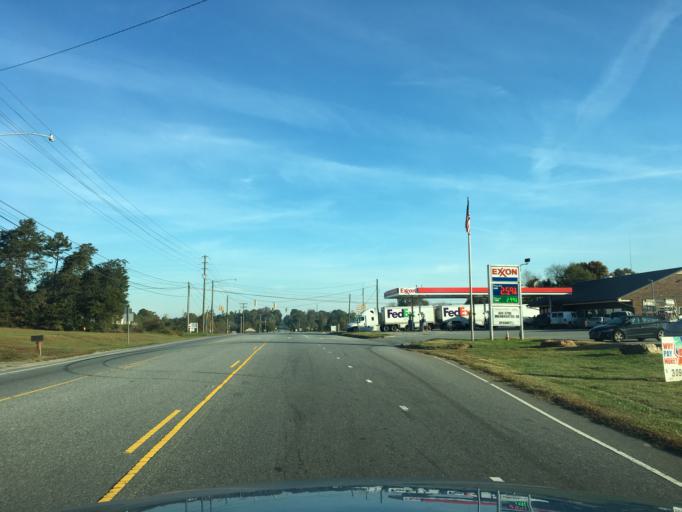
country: US
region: North Carolina
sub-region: Catawba County
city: Maiden
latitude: 35.5949
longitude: -81.2556
